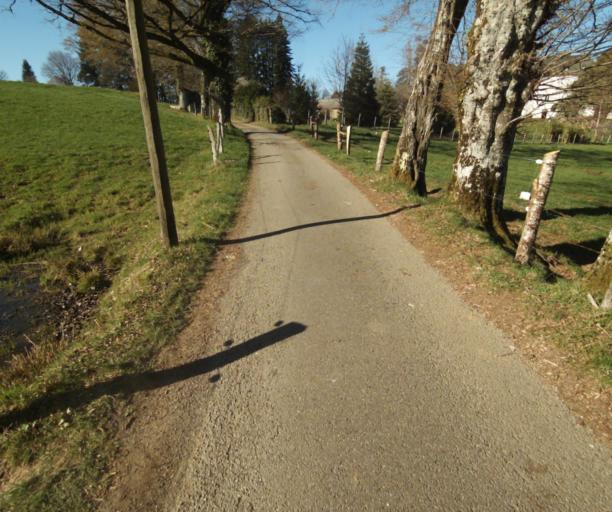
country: FR
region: Limousin
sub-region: Departement de la Correze
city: Seilhac
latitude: 45.3819
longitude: 1.7242
